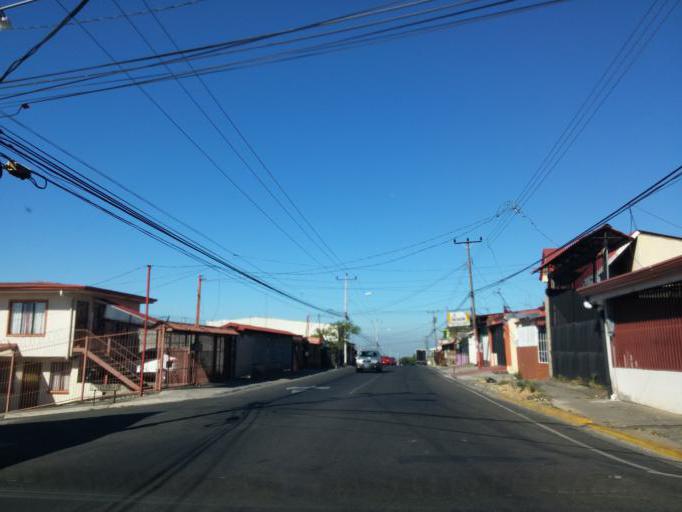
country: CR
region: Alajuela
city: Alajuela
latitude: 10.0204
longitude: -84.2237
